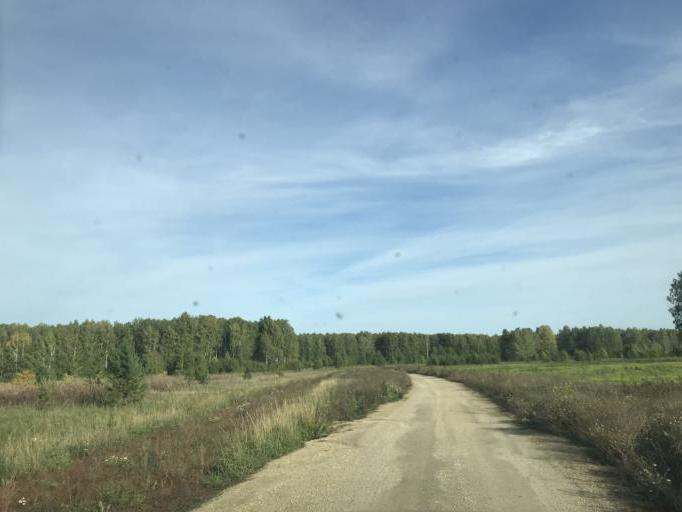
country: RU
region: Chelyabinsk
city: Poletayevo
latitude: 54.9803
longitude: 60.9654
